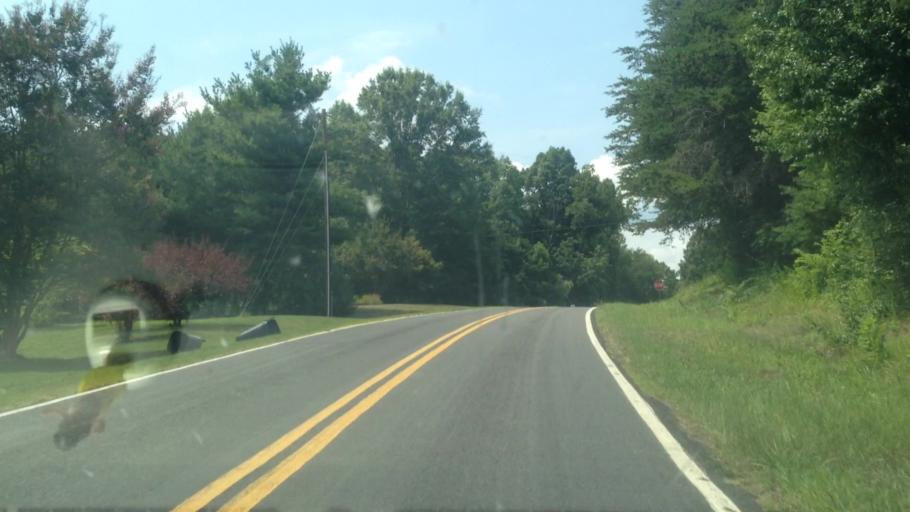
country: US
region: North Carolina
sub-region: Forsyth County
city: Walkertown
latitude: 36.2034
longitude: -80.1066
